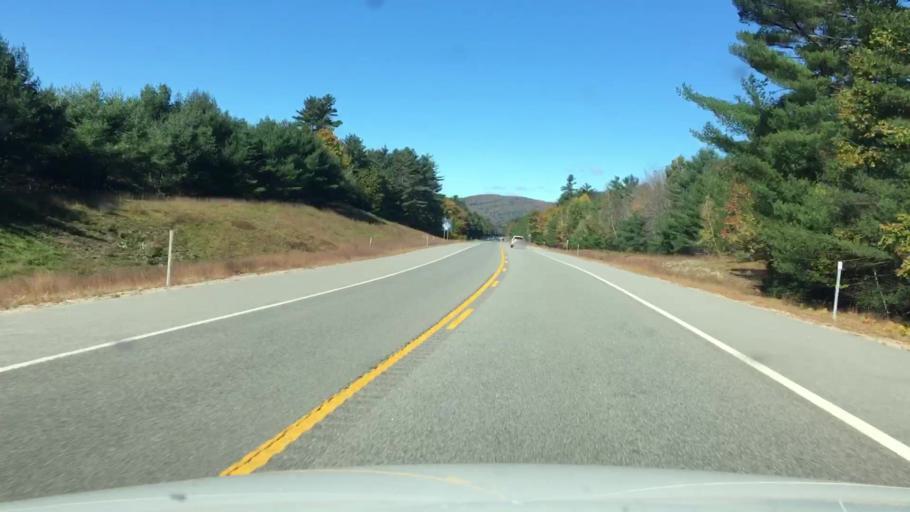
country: US
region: New Hampshire
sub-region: Carroll County
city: Sanbornville
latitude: 43.4853
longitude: -71.0077
